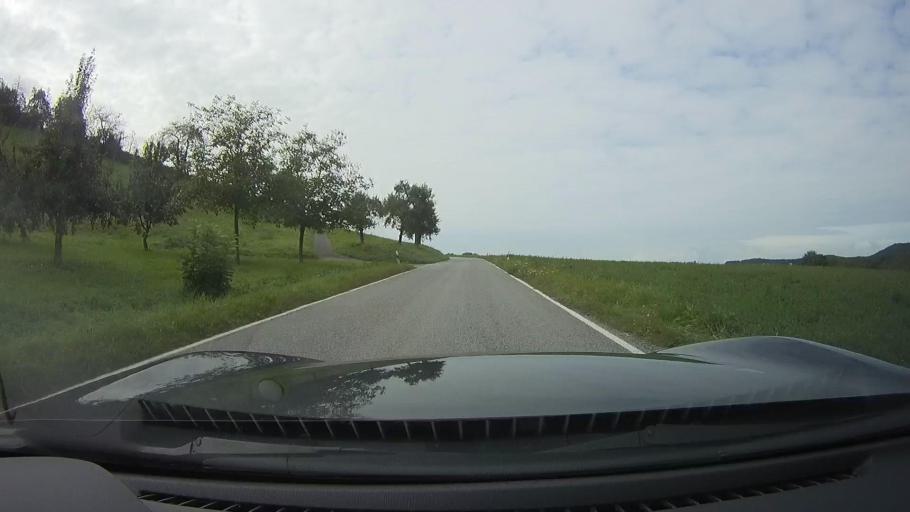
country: DE
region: Baden-Wuerttemberg
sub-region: Regierungsbezirk Stuttgart
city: Lowenstein
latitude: 49.0652
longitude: 9.3646
